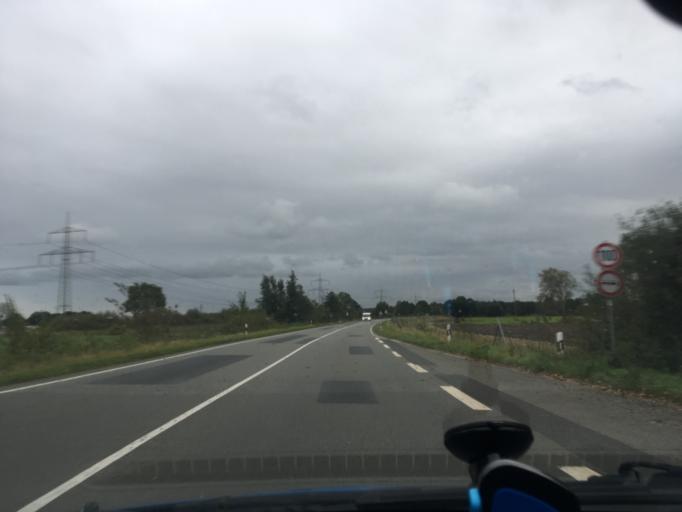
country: DE
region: Lower Saxony
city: Handorf
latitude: 53.3796
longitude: 10.3478
